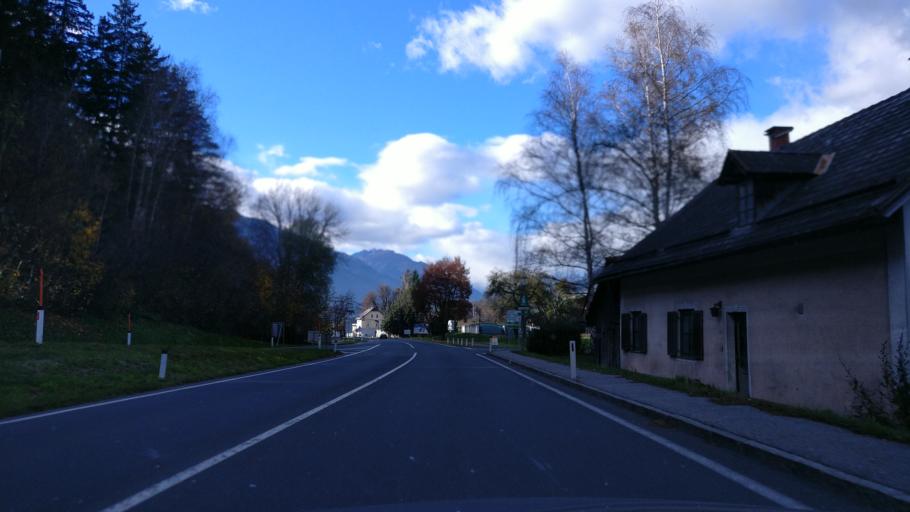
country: AT
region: Carinthia
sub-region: Politischer Bezirk Spittal an der Drau
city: Lendorf
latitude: 46.8300
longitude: 13.4279
